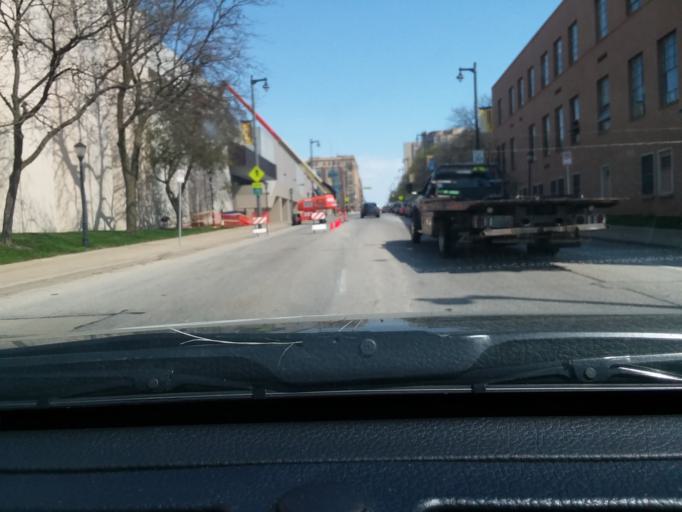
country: US
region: Wisconsin
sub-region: Milwaukee County
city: Milwaukee
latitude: 43.0362
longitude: -87.9330
